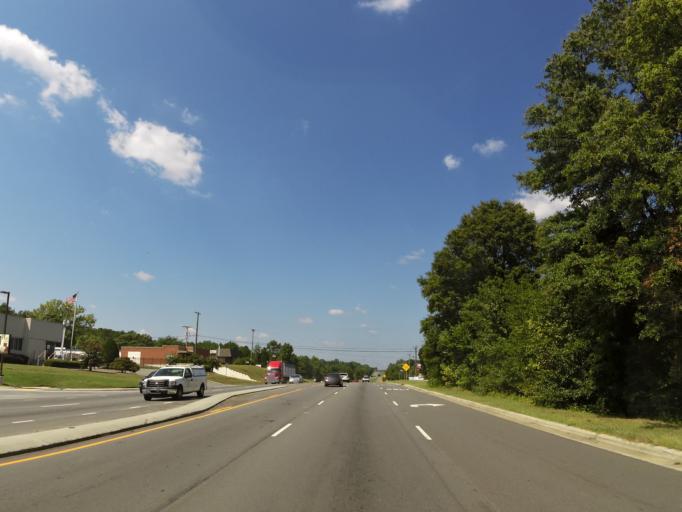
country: US
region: North Carolina
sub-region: Gaston County
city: Dallas
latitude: 35.2911
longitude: -81.1879
